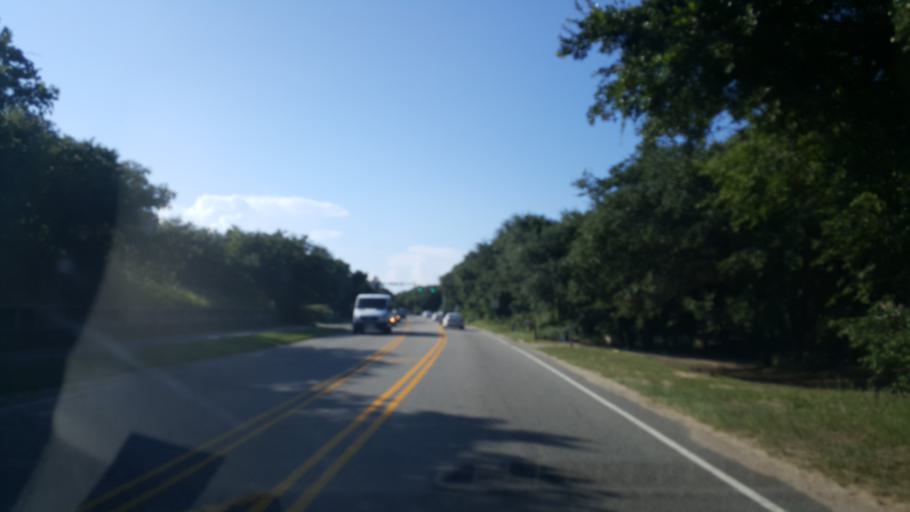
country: US
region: North Carolina
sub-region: Dare County
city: Southern Shores
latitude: 36.1276
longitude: -75.7289
